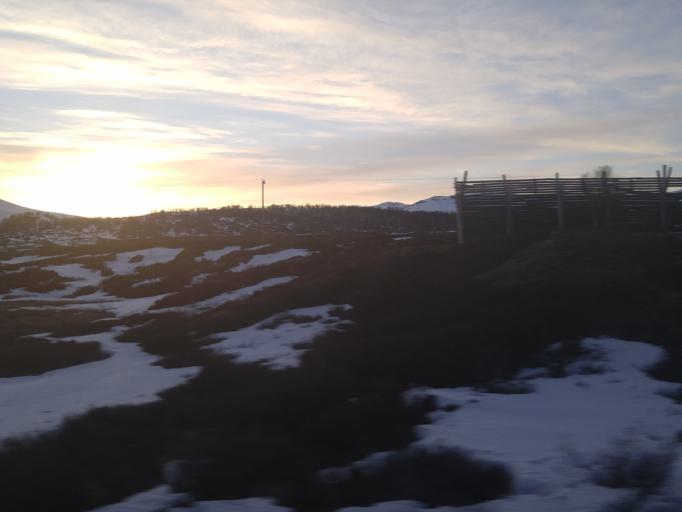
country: NO
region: Sor-Trondelag
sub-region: Oppdal
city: Oppdal
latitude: 62.2810
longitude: 9.5899
